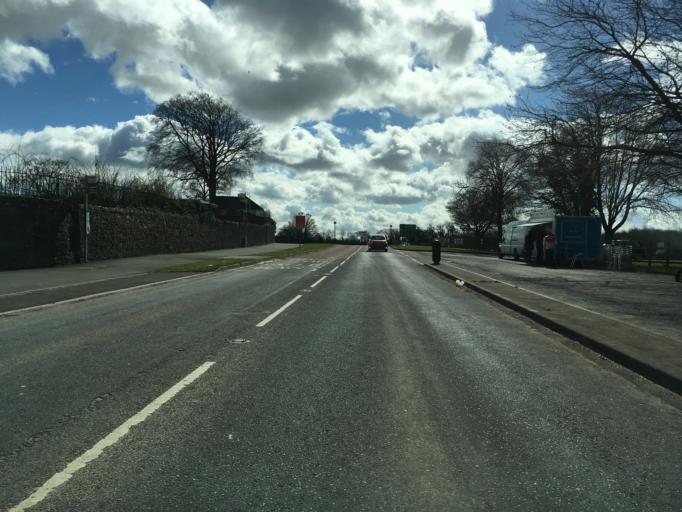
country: GB
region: Wales
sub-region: Monmouthshire
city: Chepstow
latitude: 51.6519
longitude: -2.6925
